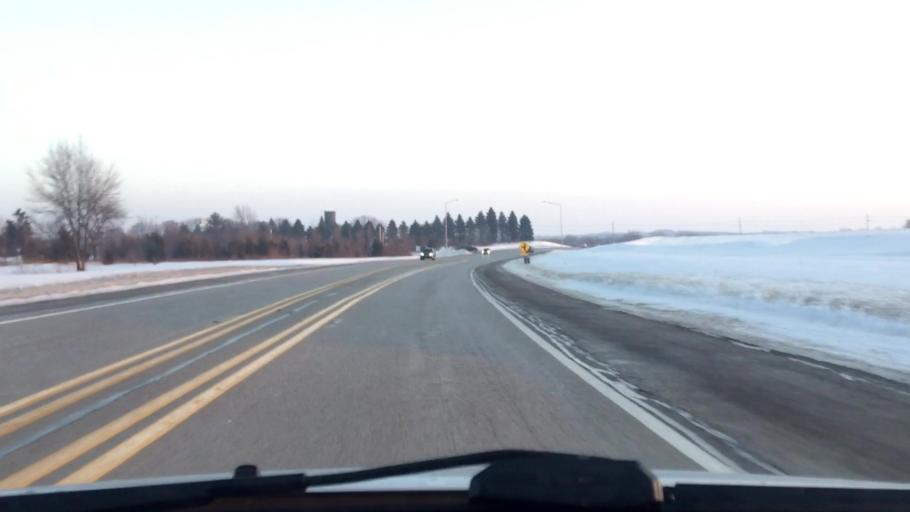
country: US
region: Illinois
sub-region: Kane County
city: Village of Campton Hills
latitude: 41.9436
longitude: -88.3992
